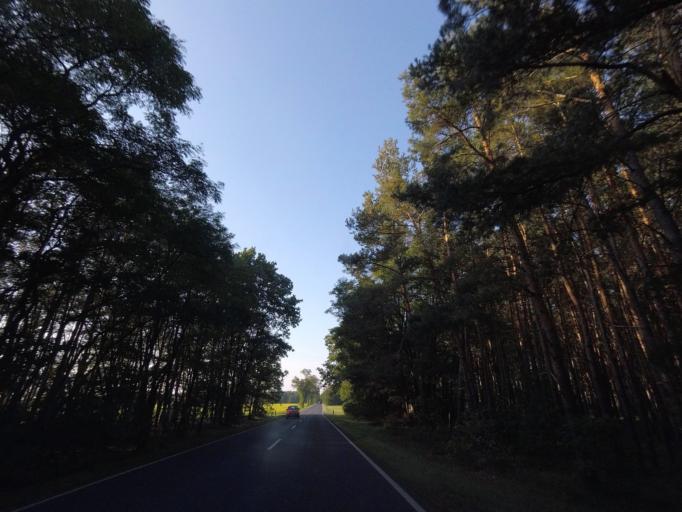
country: DE
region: Saxony-Anhalt
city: Seyda
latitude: 51.8274
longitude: 12.9082
